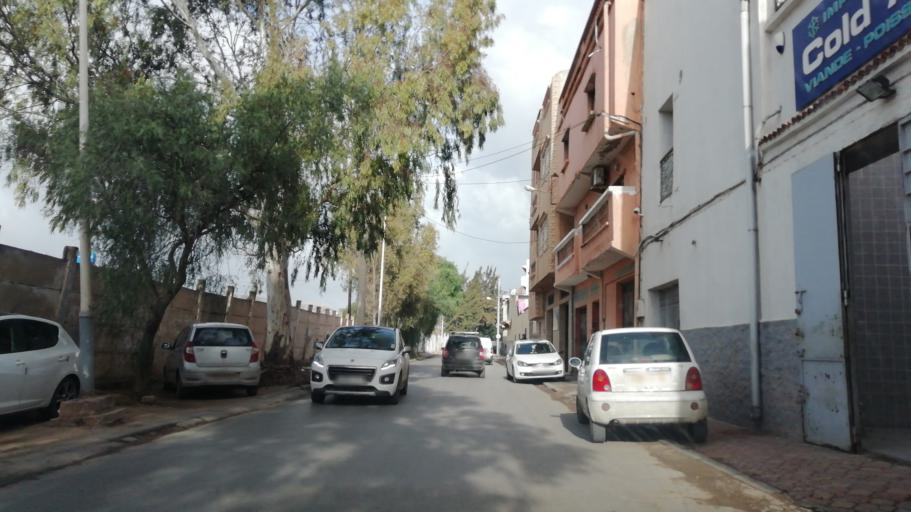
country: DZ
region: Oran
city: Oran
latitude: 35.6820
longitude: -0.6267
